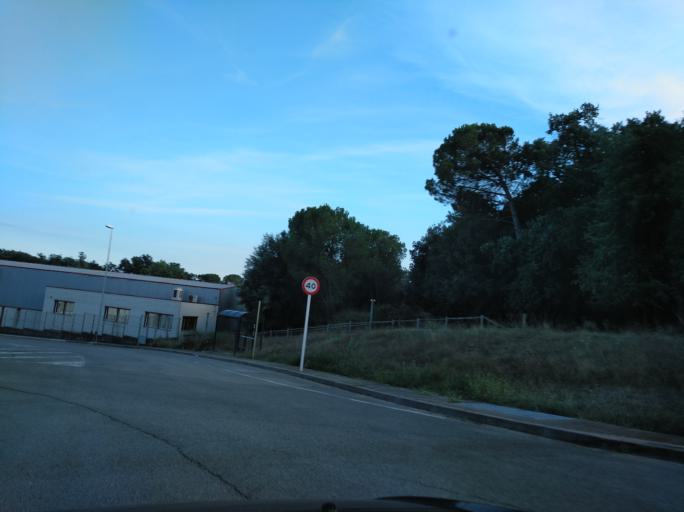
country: ES
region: Catalonia
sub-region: Provincia de Girona
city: Aiguaviva
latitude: 41.9415
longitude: 2.7764
